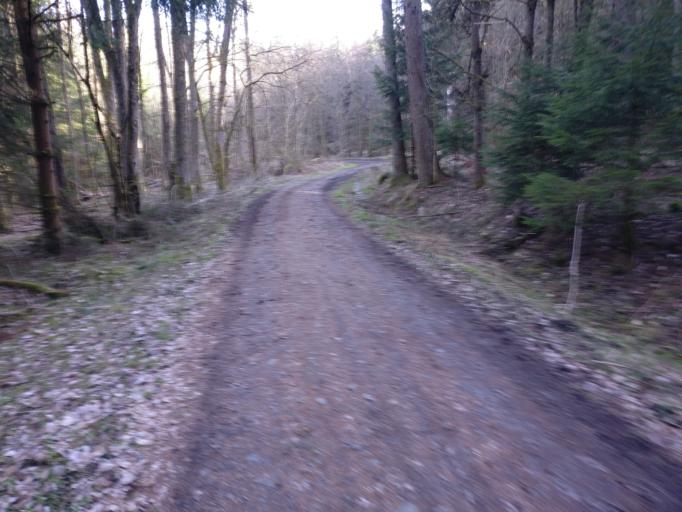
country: DE
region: Hesse
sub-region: Regierungsbezirk Giessen
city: Greifenstein
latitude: 50.6270
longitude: 8.2710
